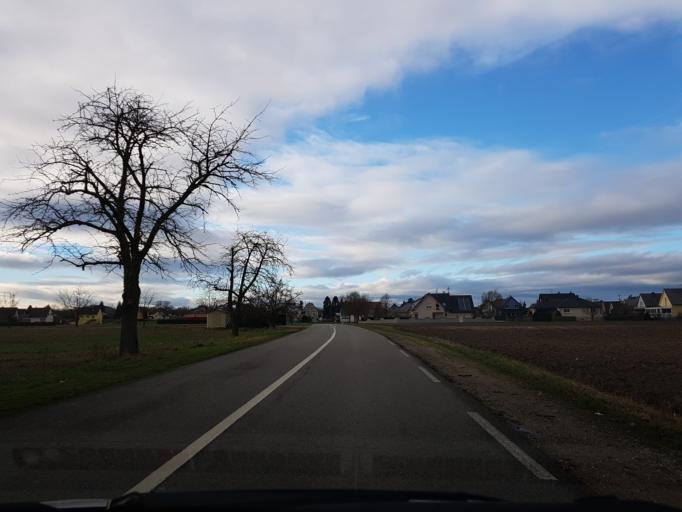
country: FR
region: Alsace
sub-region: Departement du Haut-Rhin
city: Kembs
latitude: 47.7090
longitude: 7.5114
